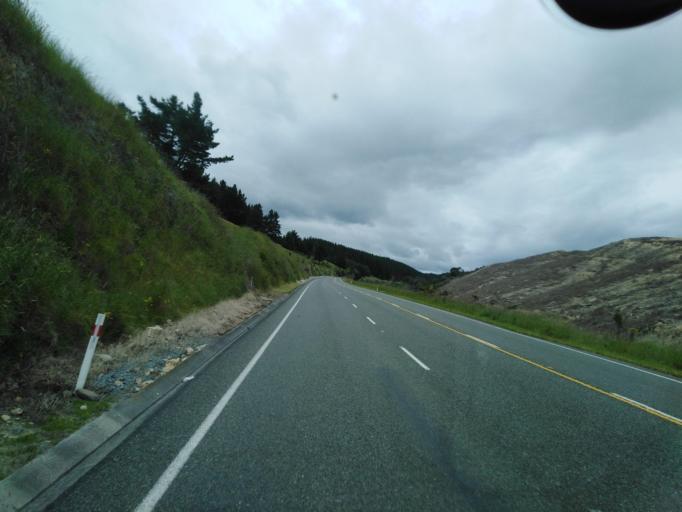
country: NZ
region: Tasman
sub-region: Tasman District
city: Wakefield
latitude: -41.4678
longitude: 172.9443
